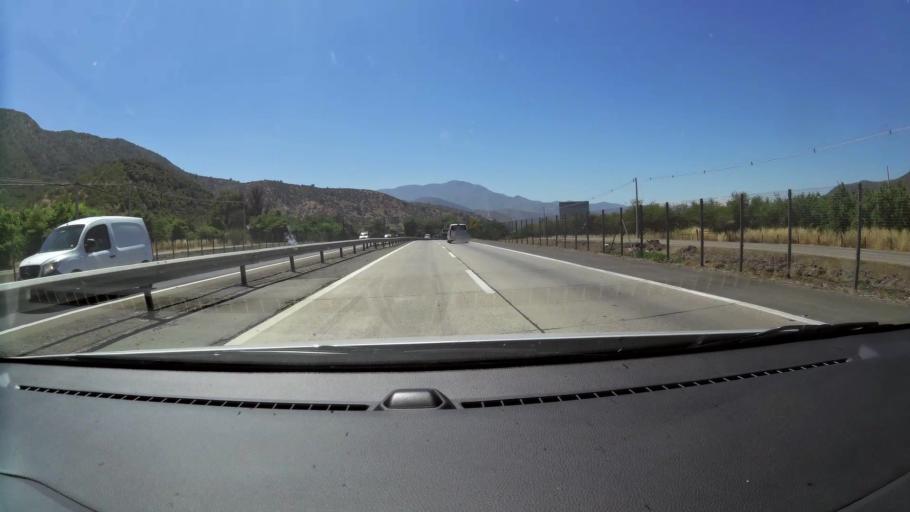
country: CL
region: Santiago Metropolitan
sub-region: Provincia de Chacabuco
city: Lampa
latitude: -33.4013
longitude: -71.1050
